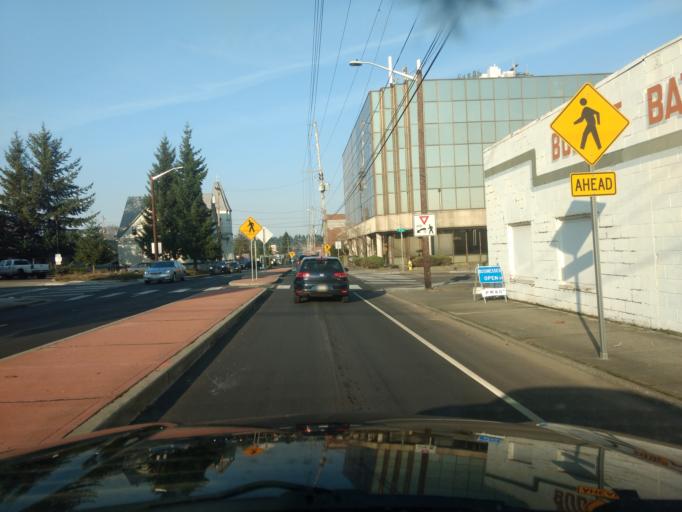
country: US
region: Washington
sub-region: Kitsap County
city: Bremerton
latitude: 47.5657
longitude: -122.6329
